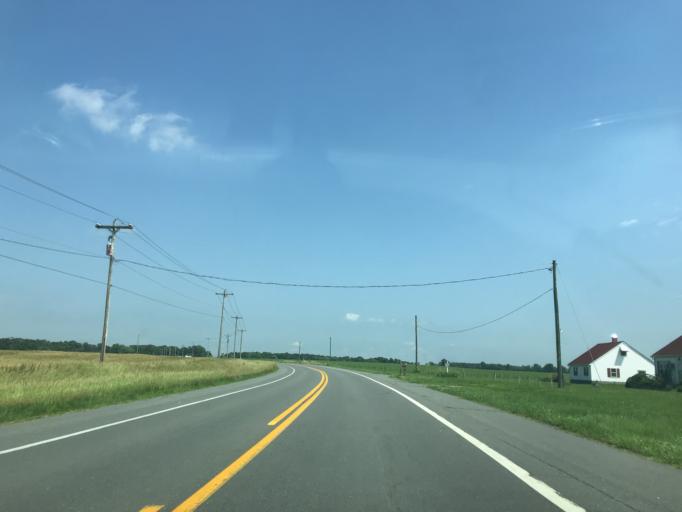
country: US
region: Maryland
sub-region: Dorchester County
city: Hurlock
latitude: 38.5935
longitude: -75.8936
